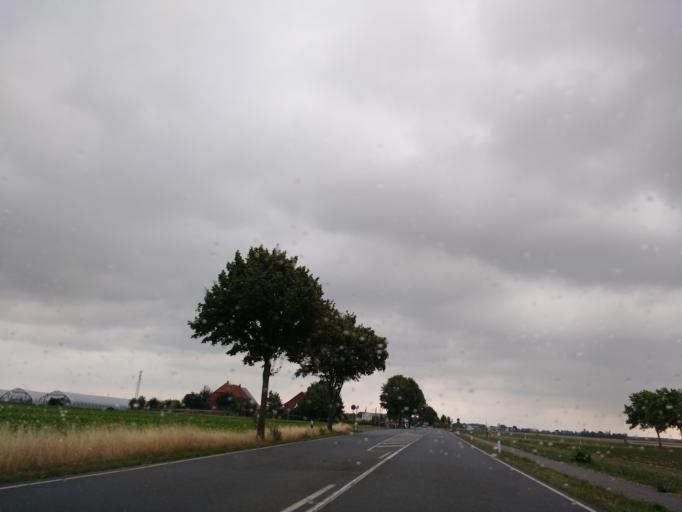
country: DE
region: Lower Saxony
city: Vechelde
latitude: 52.2577
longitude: 10.3371
